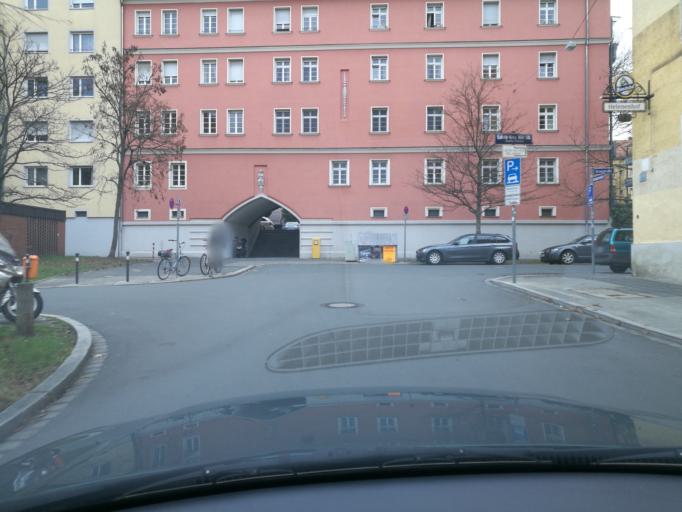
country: DE
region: Bavaria
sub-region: Regierungsbezirk Mittelfranken
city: Wetzendorf
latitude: 49.4592
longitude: 11.0536
